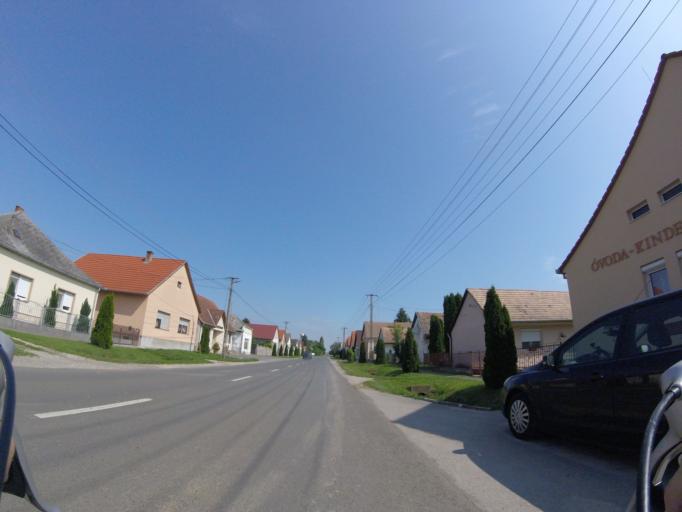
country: HU
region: Baranya
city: Siklos
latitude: 45.9380
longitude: 18.3628
